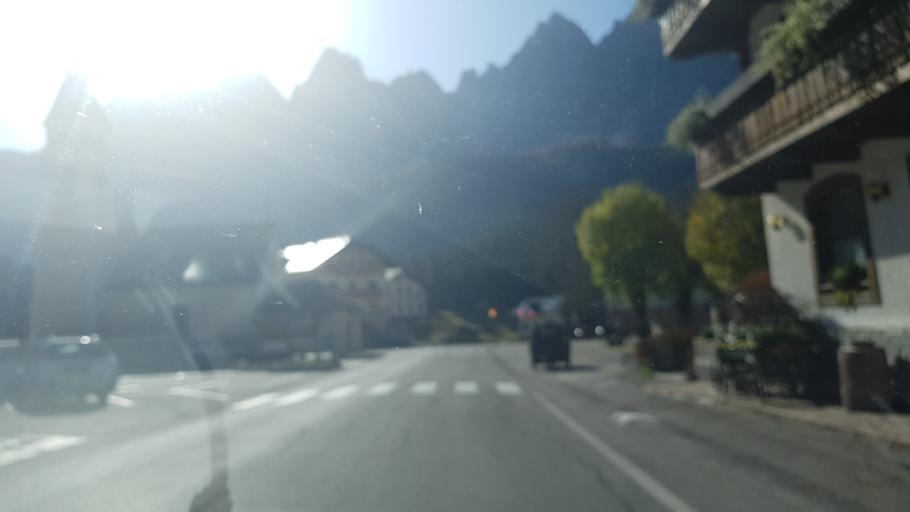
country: IT
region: Veneto
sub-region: Provincia di Belluno
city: Granvilla
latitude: 46.5697
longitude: 12.7212
